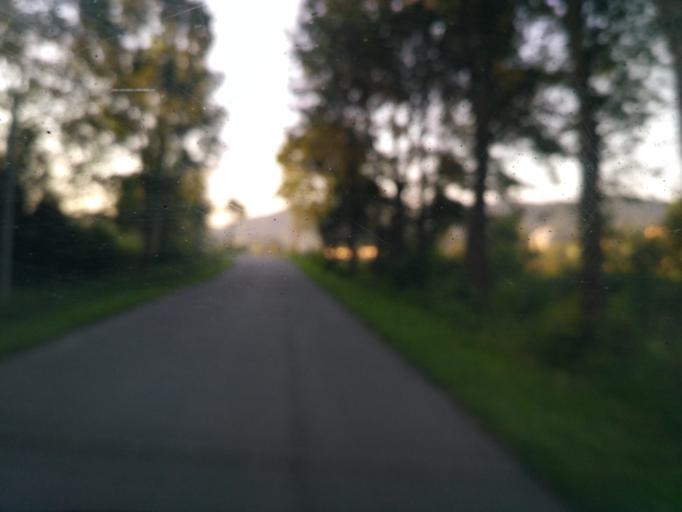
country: PL
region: Subcarpathian Voivodeship
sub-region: Powiat krosnienski
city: Odrzykon
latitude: 49.7810
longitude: 21.7638
